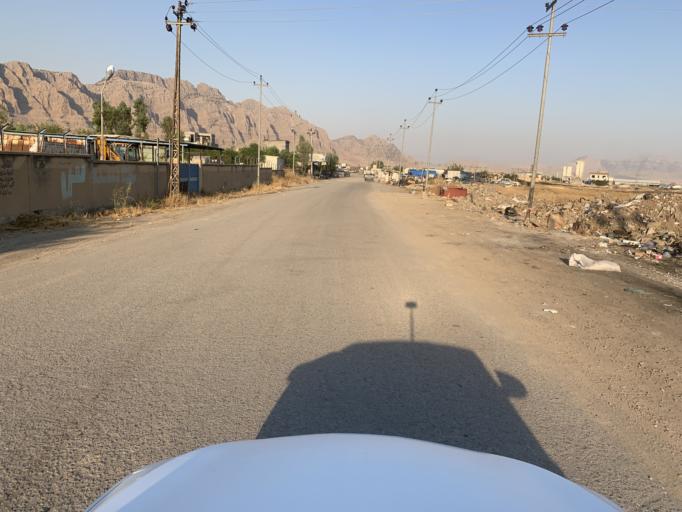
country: IQ
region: As Sulaymaniyah
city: Raniye
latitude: 36.2450
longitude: 44.8857
